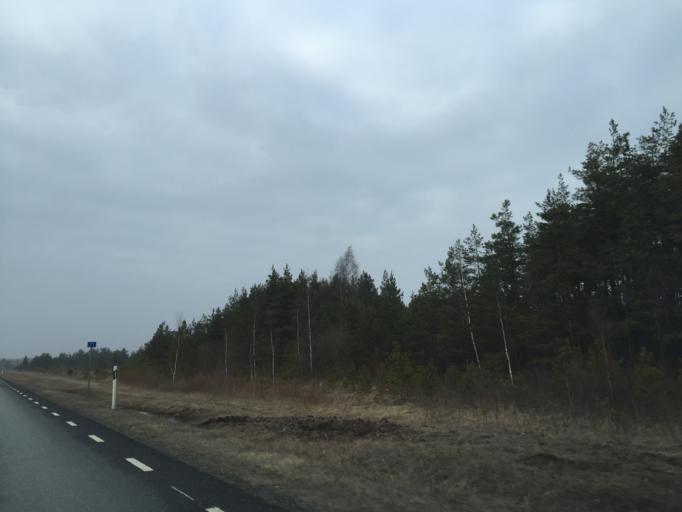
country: EE
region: Saare
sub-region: Orissaare vald
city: Orissaare
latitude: 58.5850
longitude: 23.3478
